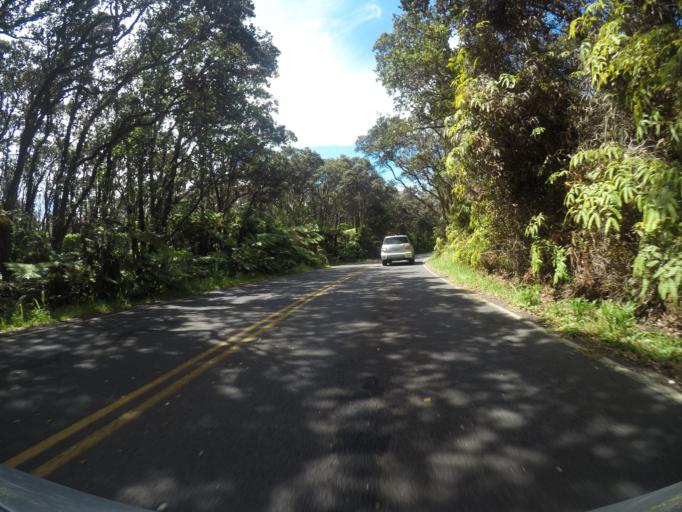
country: US
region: Hawaii
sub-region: Hawaii County
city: Volcano
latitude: 19.4185
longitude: -155.2429
